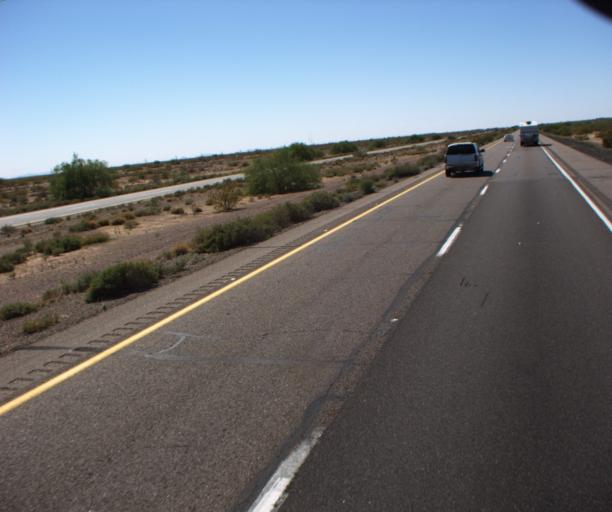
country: US
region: Arizona
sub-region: Maricopa County
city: Gila Bend
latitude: 32.9059
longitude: -112.9874
